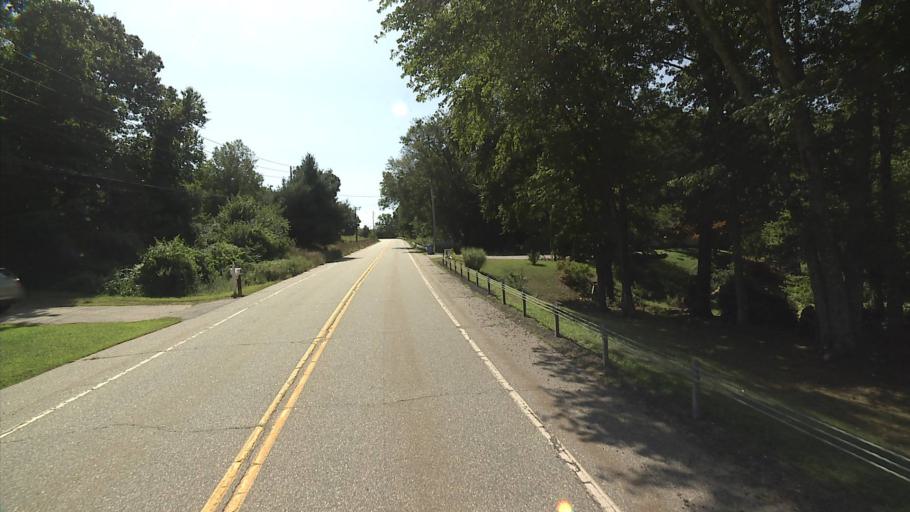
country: US
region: Connecticut
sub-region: New London County
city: Baltic
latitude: 41.6322
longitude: -72.1283
